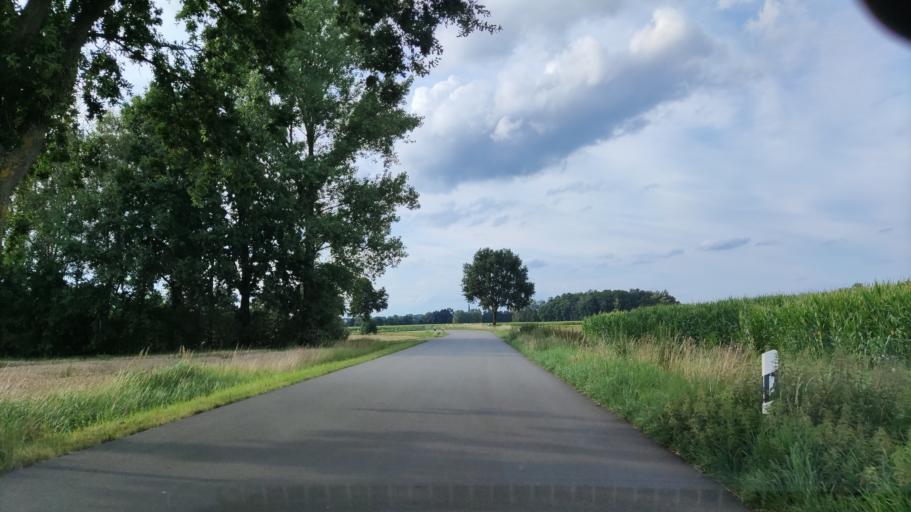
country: DE
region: Lower Saxony
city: Dannenberg
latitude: 53.0863
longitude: 11.1022
